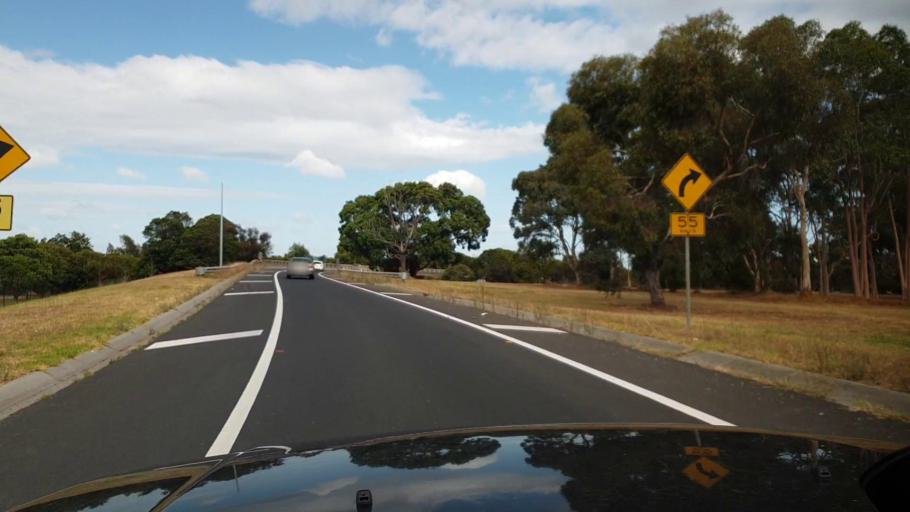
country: AU
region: Victoria
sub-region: Monash
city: Mulgrave
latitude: -37.9215
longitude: 145.1775
